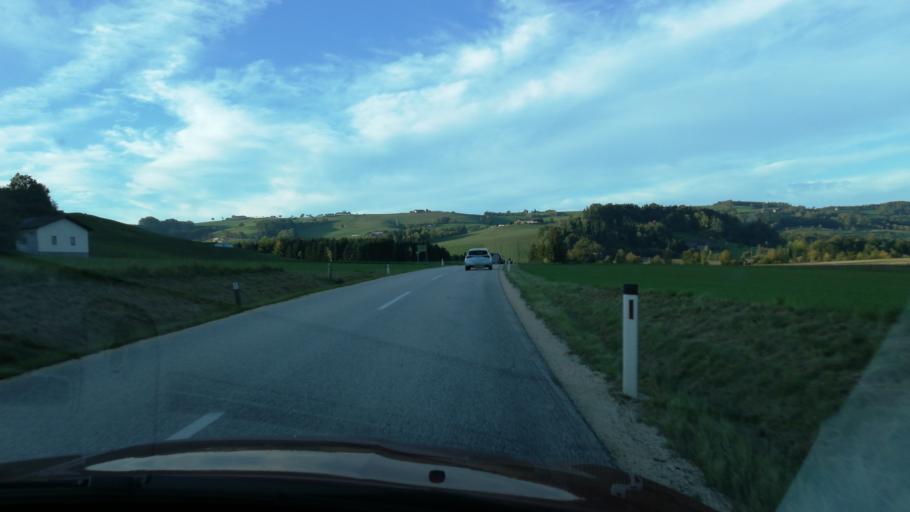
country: AT
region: Upper Austria
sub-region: Politischer Bezirk Steyr-Land
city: Ternberg
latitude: 47.9661
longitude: 14.3451
